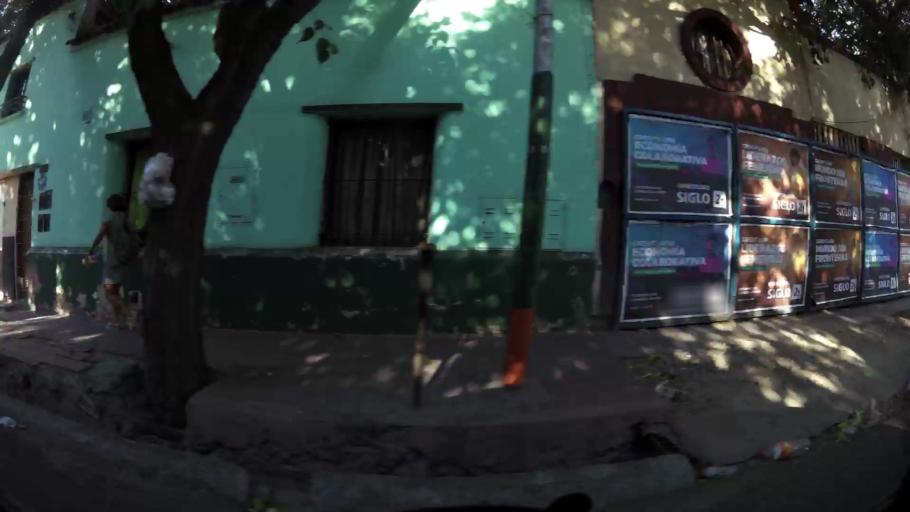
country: AR
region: Mendoza
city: Mendoza
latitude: -32.9058
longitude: -68.8287
